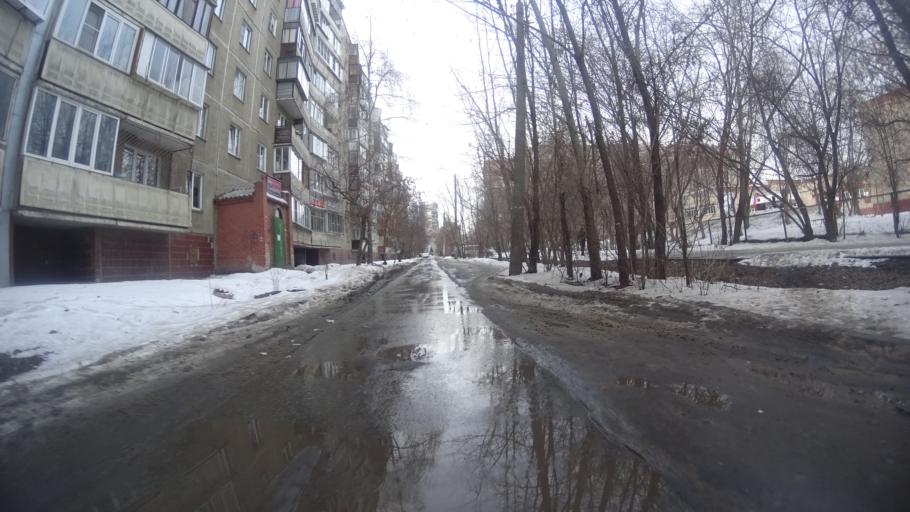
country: RU
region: Chelyabinsk
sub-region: Gorod Chelyabinsk
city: Chelyabinsk
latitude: 55.1758
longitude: 61.3471
